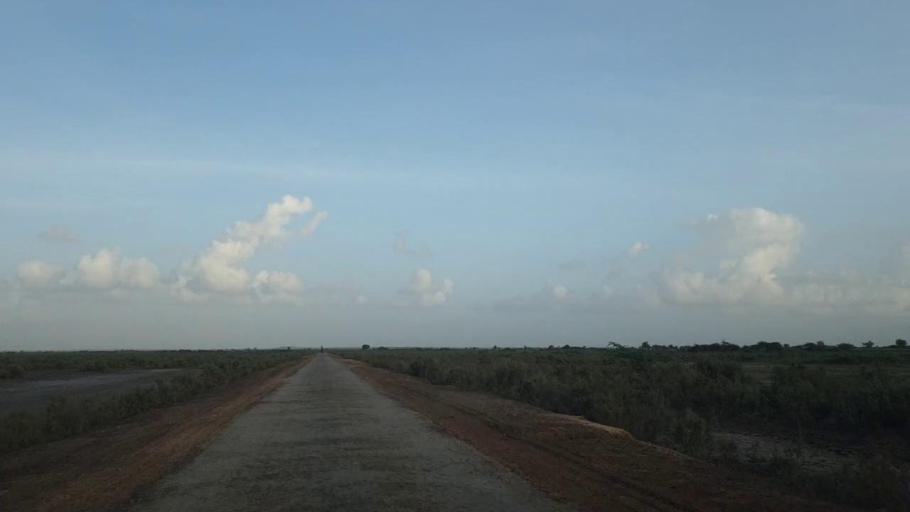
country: PK
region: Sindh
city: Kadhan
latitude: 24.5690
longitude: 69.1181
